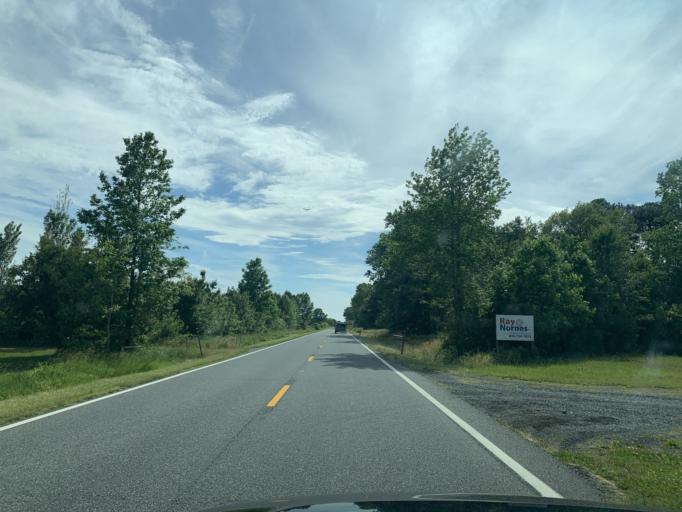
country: US
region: Maryland
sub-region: Worcester County
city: Berlin
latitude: 38.3174
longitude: -75.3009
